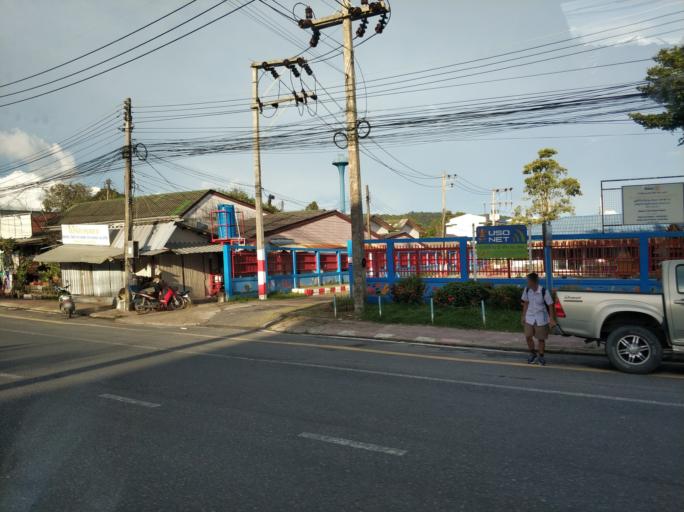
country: TH
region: Phuket
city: Kathu
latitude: 7.9039
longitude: 98.3358
